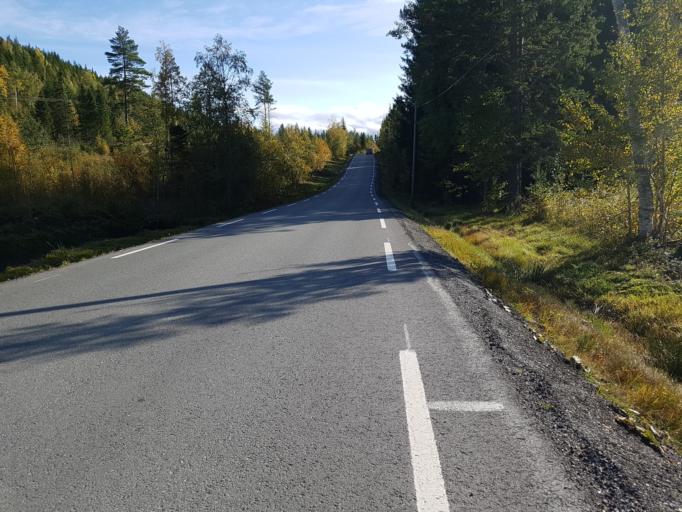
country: NO
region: Sor-Trondelag
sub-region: Malvik
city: Malvik
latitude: 63.3717
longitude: 10.6141
